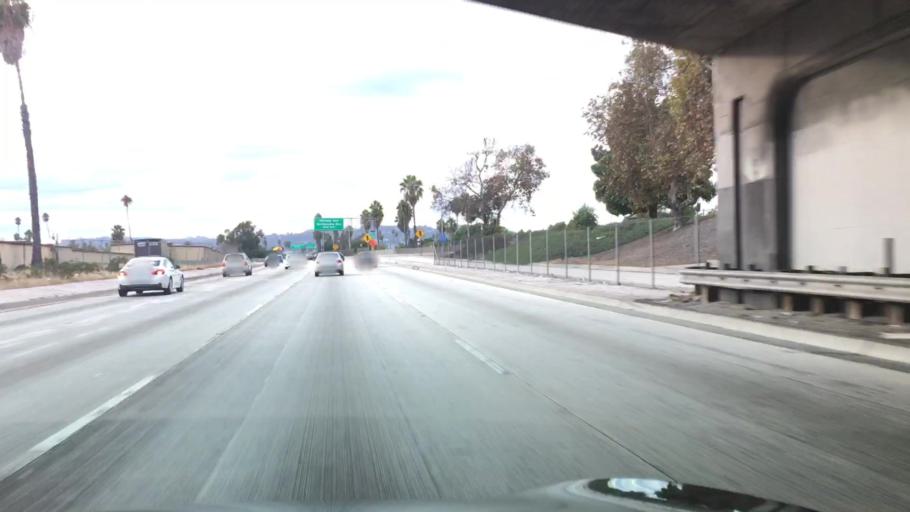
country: US
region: California
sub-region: Los Angeles County
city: Silver Lake
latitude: 34.0803
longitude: -118.2920
